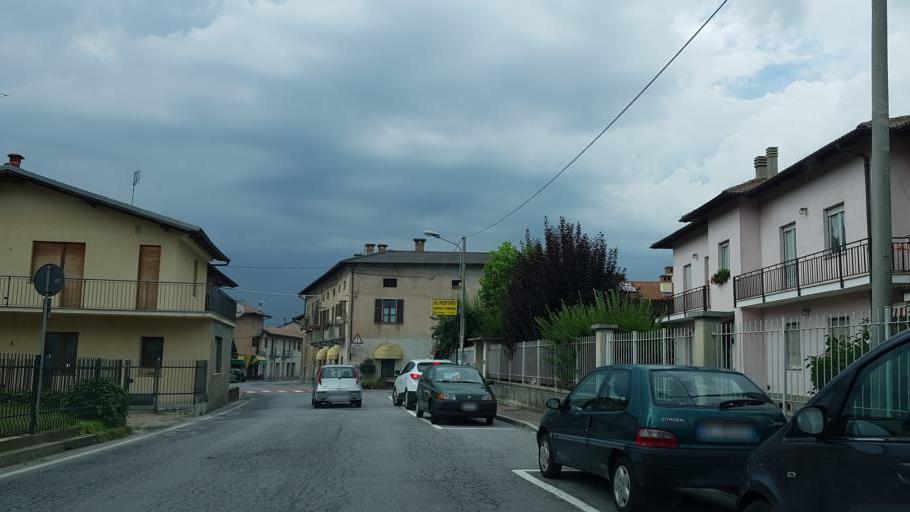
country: IT
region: Piedmont
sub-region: Provincia di Cuneo
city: Cervasca
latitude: 44.3817
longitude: 7.4696
